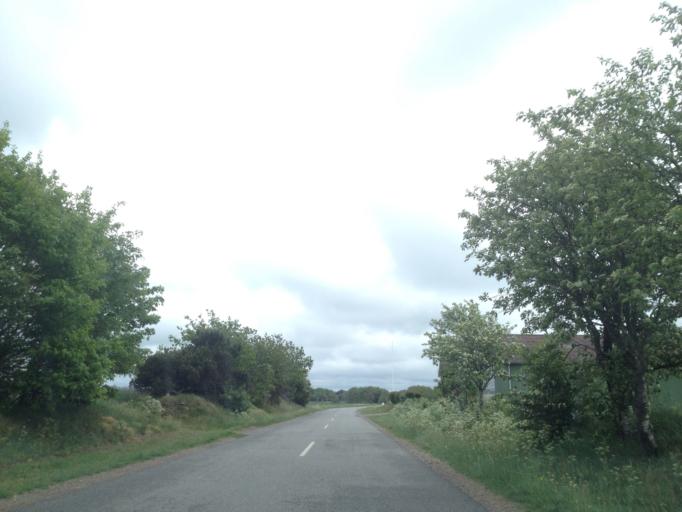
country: DK
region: South Denmark
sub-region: Tonder Kommune
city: Sherrebek
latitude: 55.0861
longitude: 8.7642
